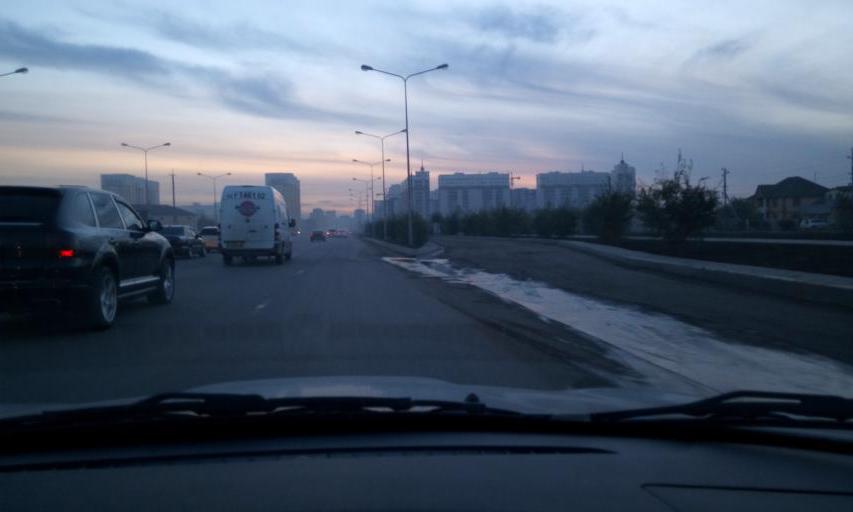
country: KZ
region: Astana Qalasy
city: Astana
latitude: 51.1335
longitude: 71.5128
